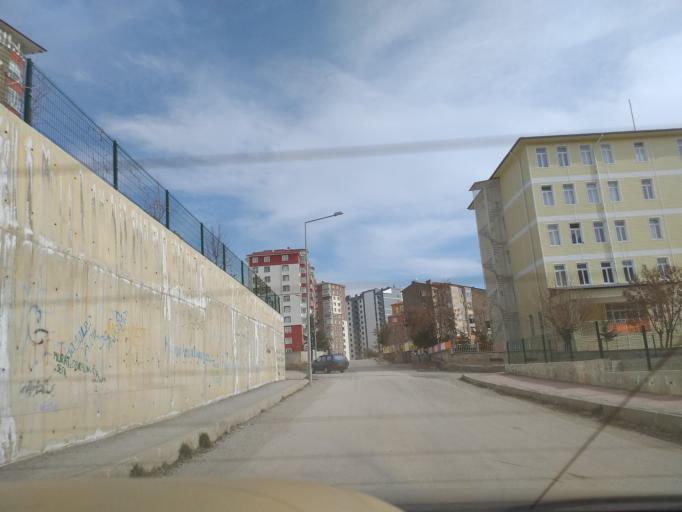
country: TR
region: Yozgat
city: Yozgat
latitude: 39.8307
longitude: 34.8204
